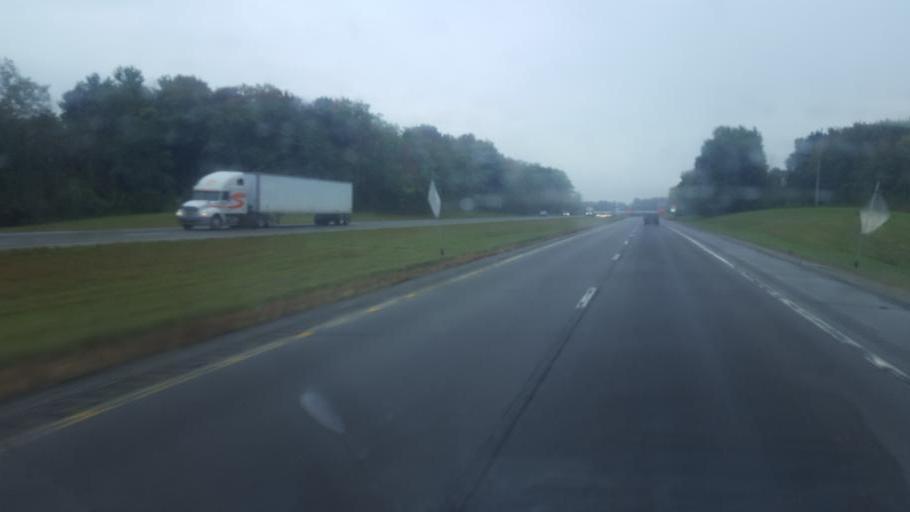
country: US
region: Ohio
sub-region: Richland County
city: Ontario
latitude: 40.7799
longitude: -82.5771
